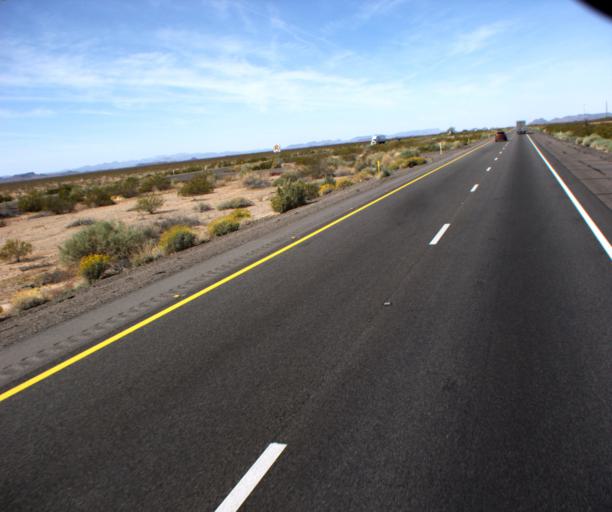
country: US
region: Arizona
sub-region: La Paz County
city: Salome
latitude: 33.5826
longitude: -113.4414
